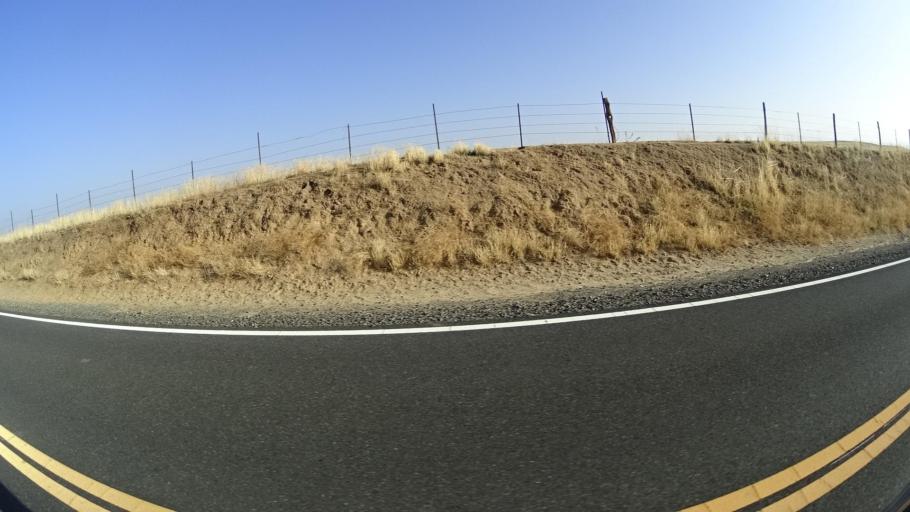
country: US
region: California
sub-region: Tulare County
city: Richgrove
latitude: 35.7478
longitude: -118.9839
